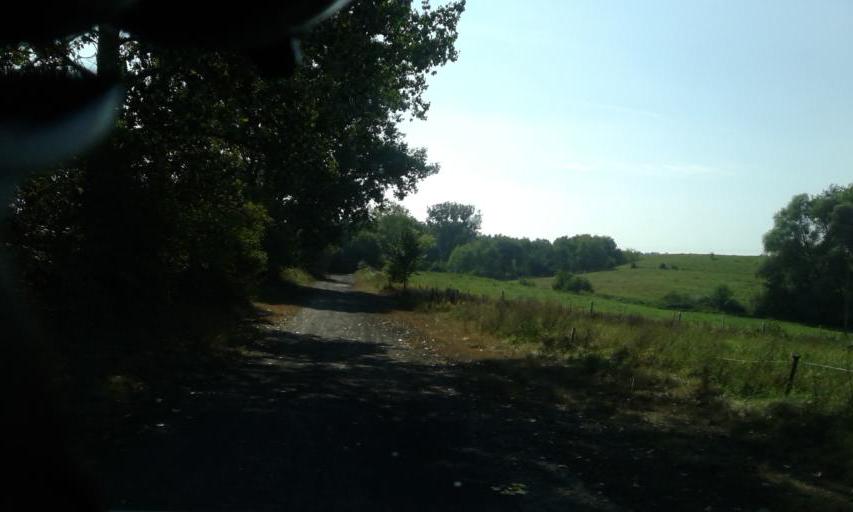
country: PL
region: West Pomeranian Voivodeship
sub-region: Powiat choszczenski
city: Krzecin
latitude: 53.0788
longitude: 15.5565
